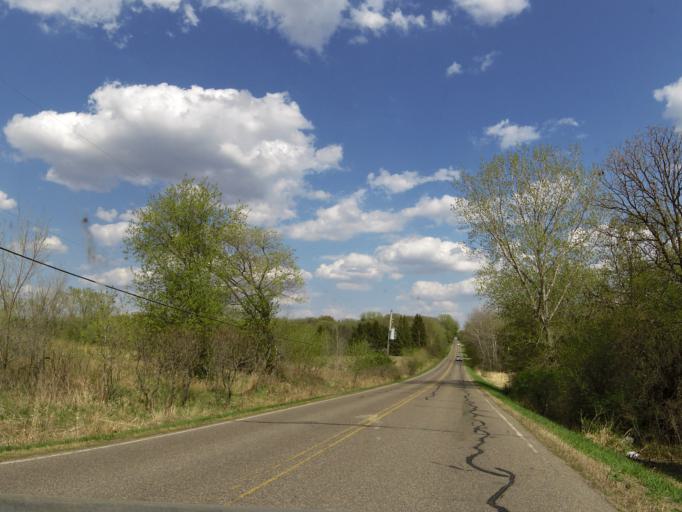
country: US
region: Minnesota
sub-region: Washington County
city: Lake Elmo
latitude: 44.9927
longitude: -92.8352
